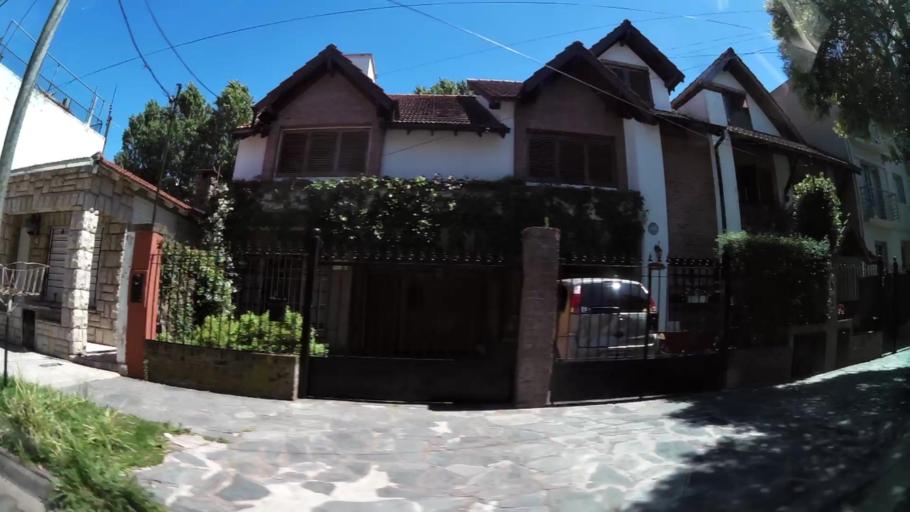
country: AR
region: Buenos Aires
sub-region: Partido de San Isidro
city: San Isidro
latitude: -34.4700
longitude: -58.5227
